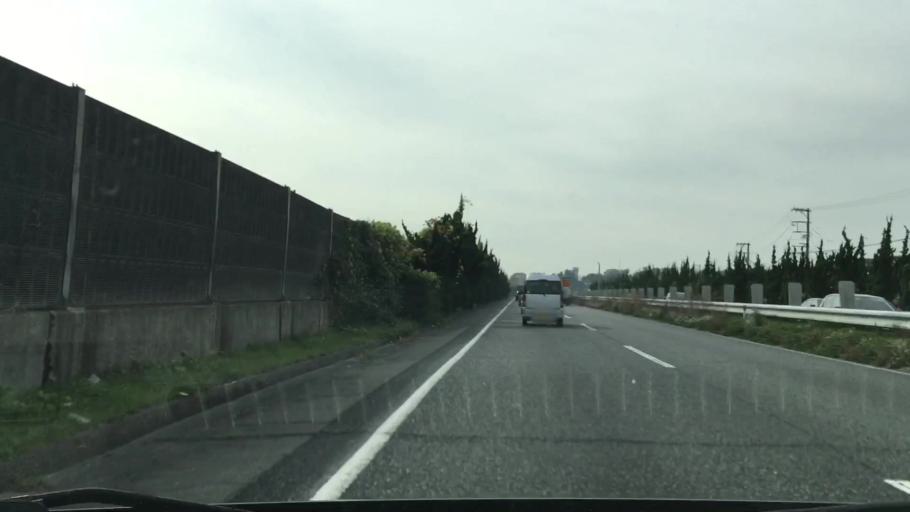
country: JP
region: Hiroshima
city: Hatsukaichi
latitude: 34.3785
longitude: 132.3472
